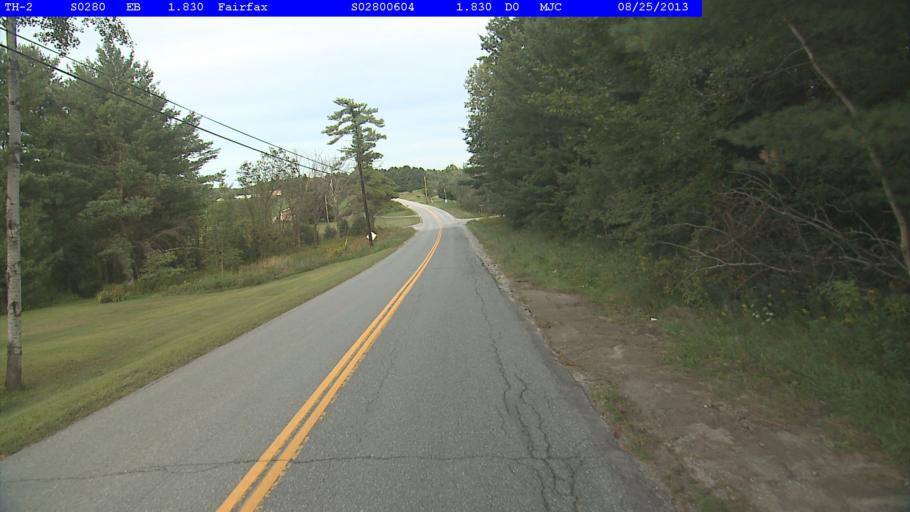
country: US
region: Vermont
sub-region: Chittenden County
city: Milton
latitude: 44.6711
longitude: -72.9753
